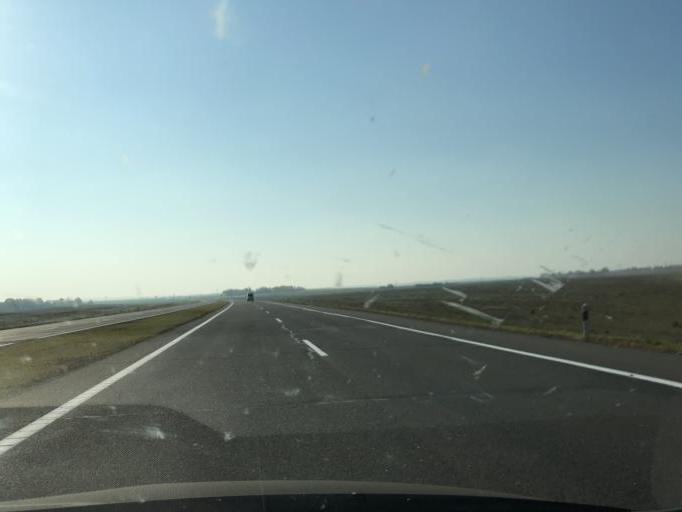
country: BY
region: Minsk
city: Snow
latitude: 53.2894
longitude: 26.3395
